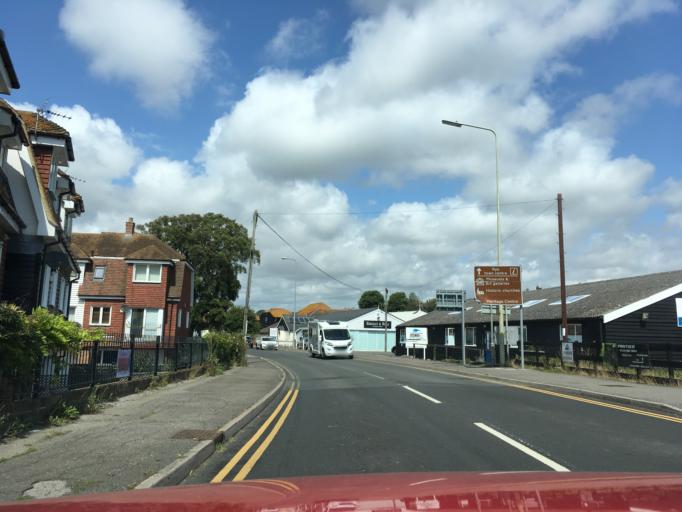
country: GB
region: England
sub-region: East Sussex
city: Rye
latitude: 50.9470
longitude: 0.7305
